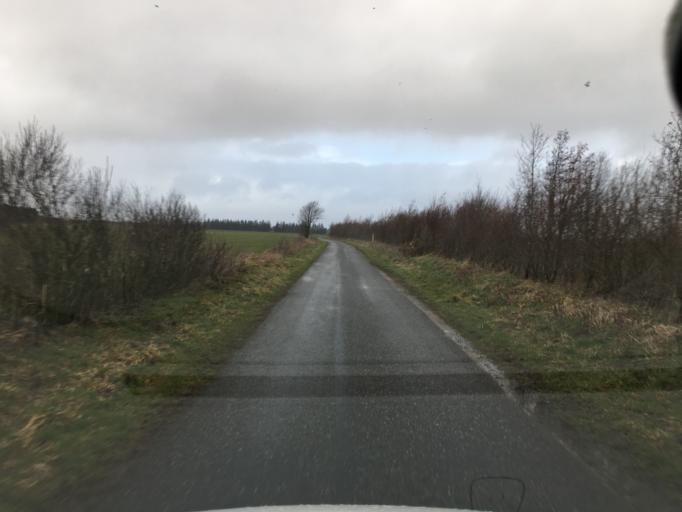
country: DK
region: South Denmark
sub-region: Aabenraa Kommune
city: Tinglev
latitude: 54.9479
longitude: 9.1608
